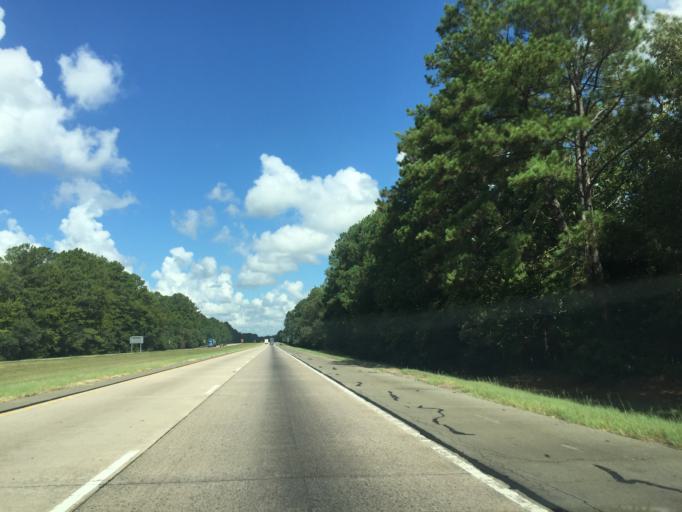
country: US
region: Georgia
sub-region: Bryan County
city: Pembroke
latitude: 32.1948
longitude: -81.4779
